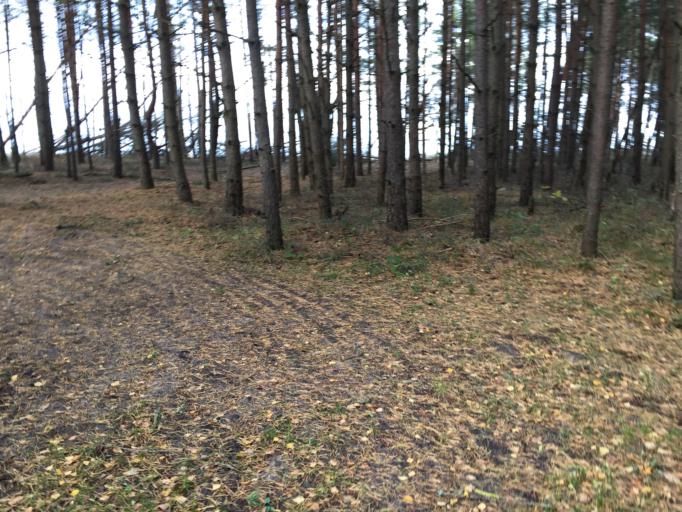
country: LV
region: Carnikava
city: Carnikava
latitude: 57.1534
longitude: 24.2561
